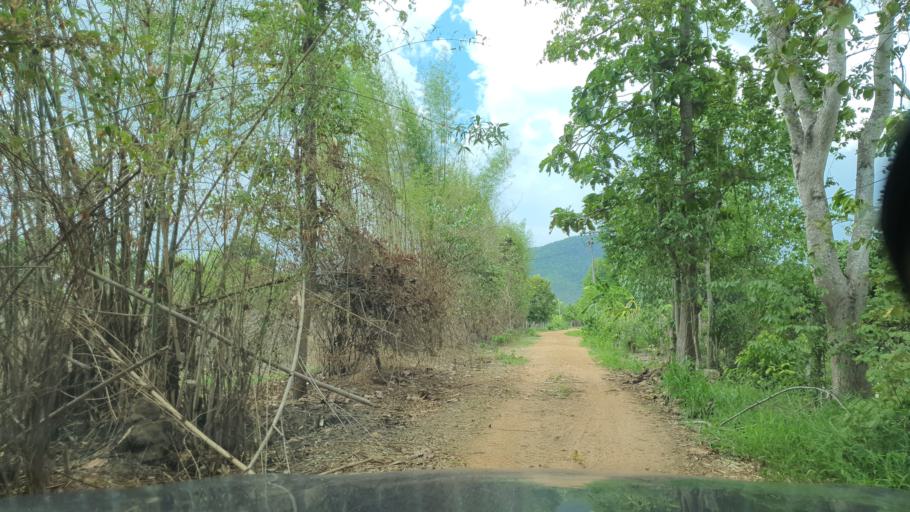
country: TH
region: Chiang Mai
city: Mae Taeng
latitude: 19.1345
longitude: 99.0345
